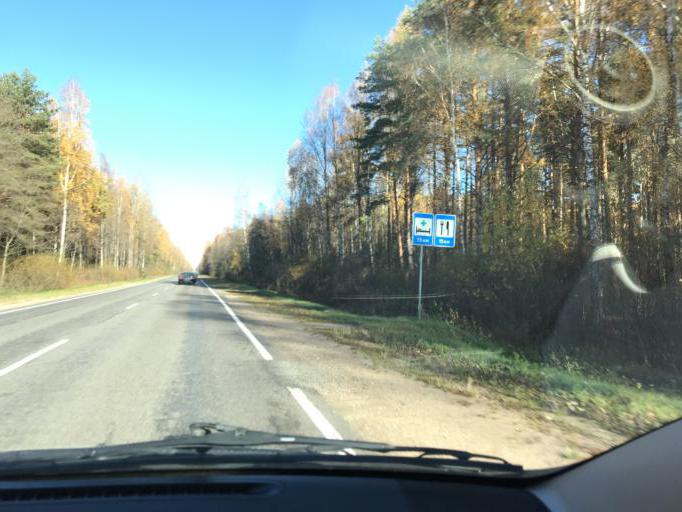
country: BY
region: Vitebsk
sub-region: Ushatski Rayon
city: Ushachy
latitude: 55.0607
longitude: 28.7527
